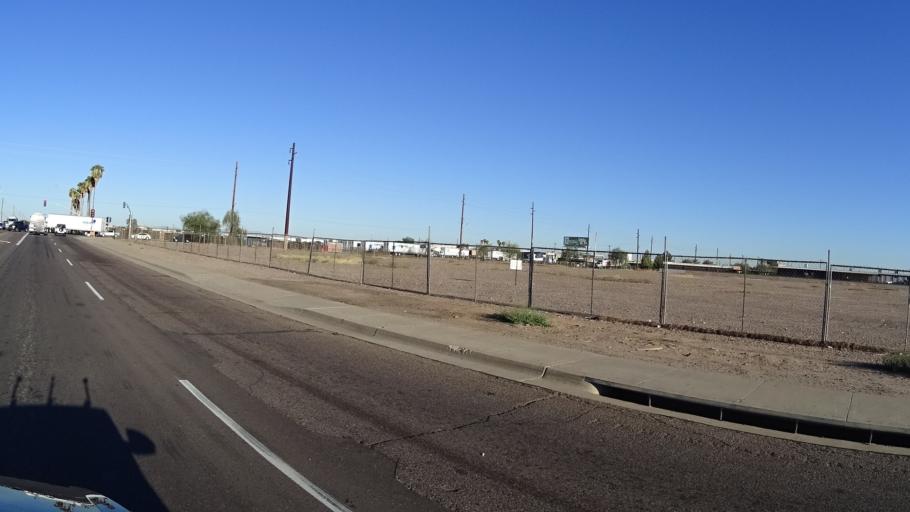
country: US
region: Arizona
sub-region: Maricopa County
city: Tolleson
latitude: 33.4370
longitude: -112.1853
